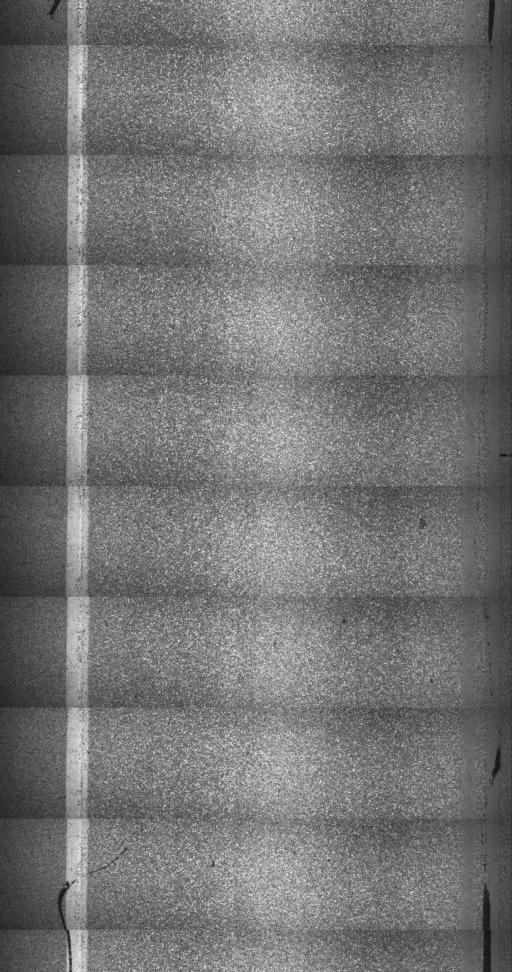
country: US
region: Vermont
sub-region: Chittenden County
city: Milton
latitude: 44.6554
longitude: -73.0092
